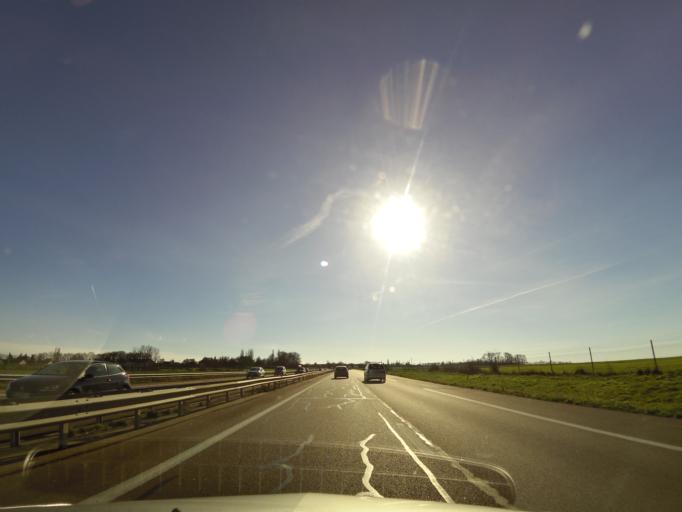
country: FR
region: Bourgogne
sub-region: Departement de l'Yonne
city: Venoy
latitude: 47.8230
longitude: 3.6236
